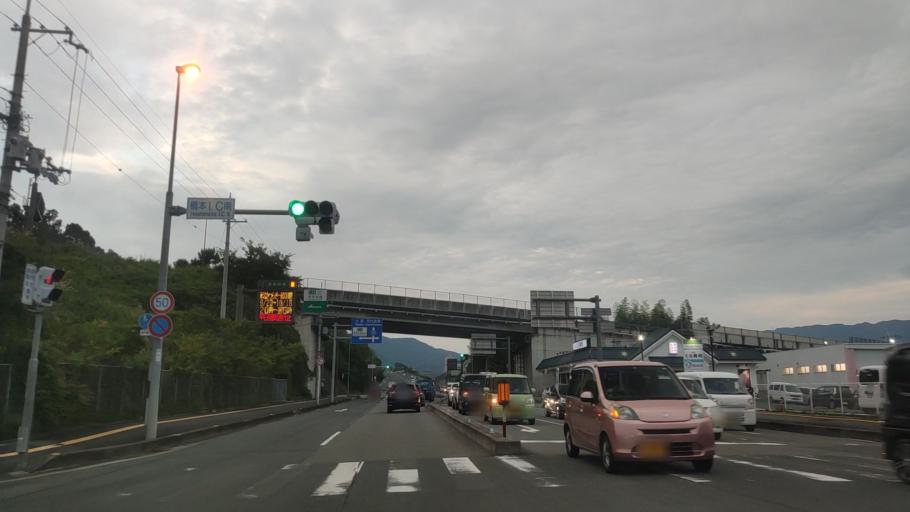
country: JP
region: Wakayama
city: Hashimoto
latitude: 34.3224
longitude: 135.6061
